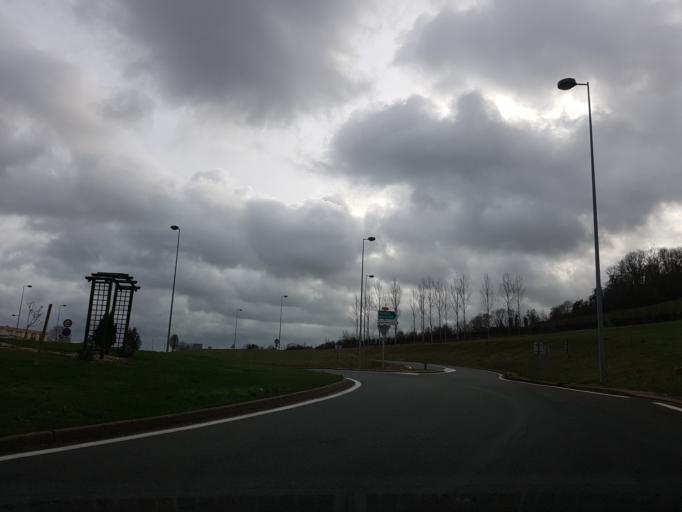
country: FR
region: Champagne-Ardenne
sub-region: Departement de la Haute-Marne
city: Langres
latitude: 47.8705
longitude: 5.3400
